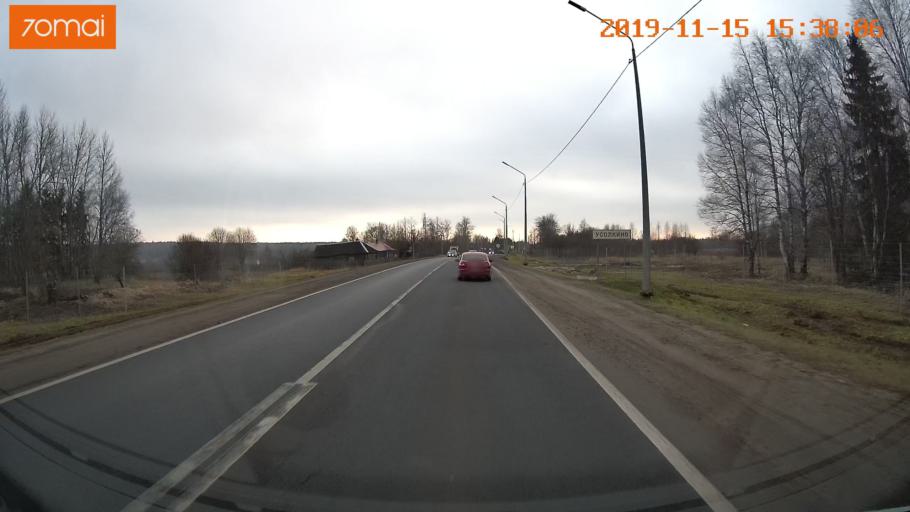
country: RU
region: Jaroslavl
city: Danilov
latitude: 58.0327
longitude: 40.0836
